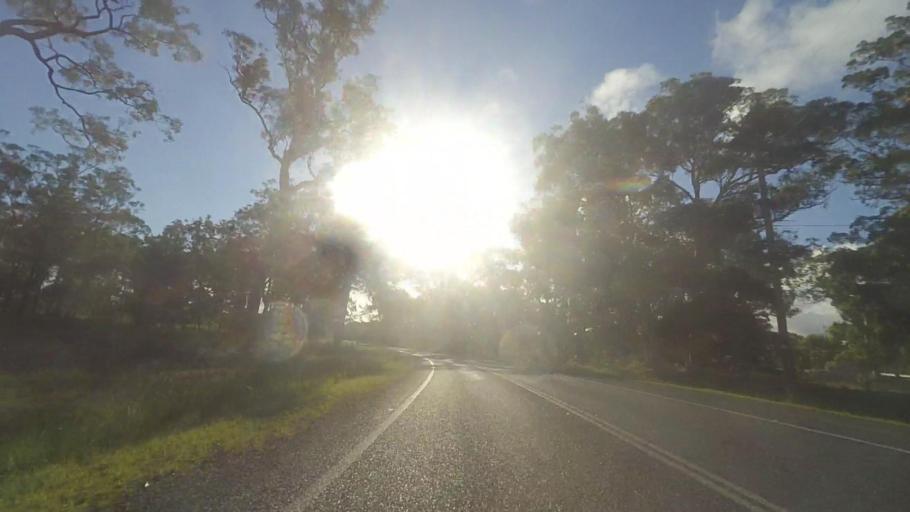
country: AU
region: New South Wales
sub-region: Great Lakes
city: Nabiac
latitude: -32.0910
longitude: 152.4574
